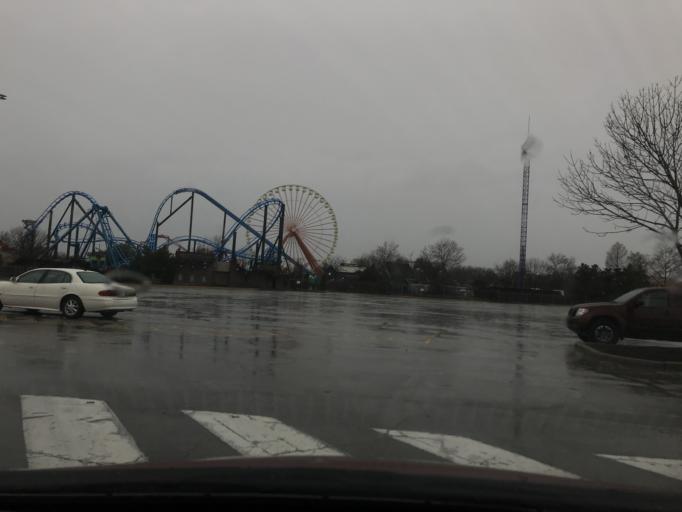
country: US
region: Kentucky
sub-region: Jefferson County
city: Audubon Park
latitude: 38.1974
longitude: -85.7427
